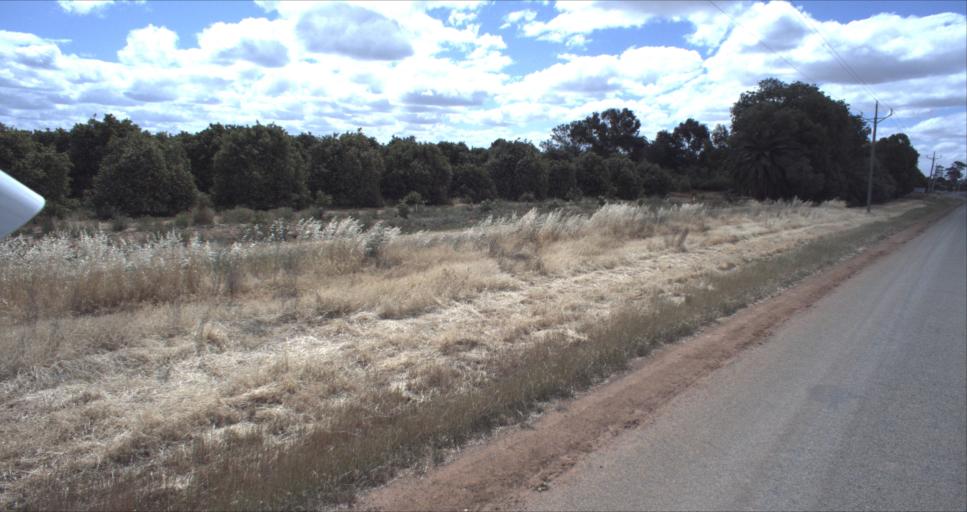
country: AU
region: New South Wales
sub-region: Leeton
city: Leeton
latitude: -34.5835
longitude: 146.3965
